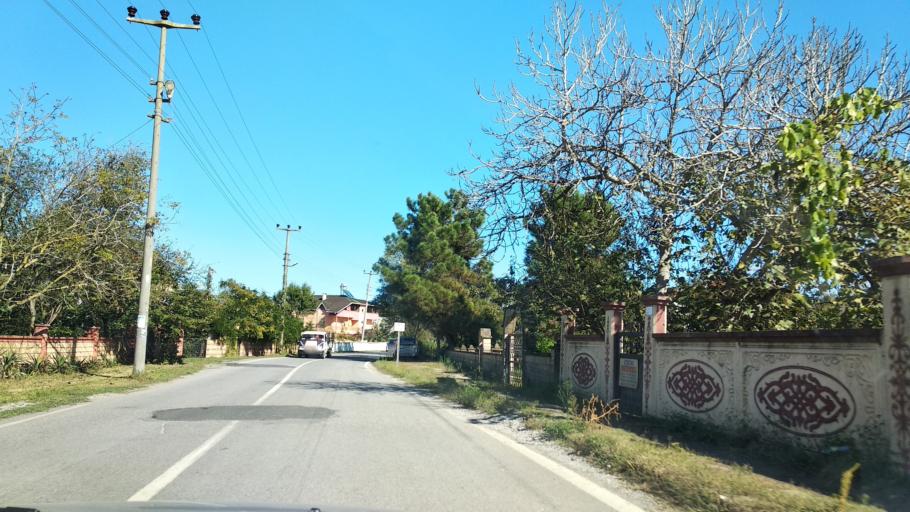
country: TR
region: Sakarya
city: Karasu
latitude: 41.1185
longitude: 30.6397
